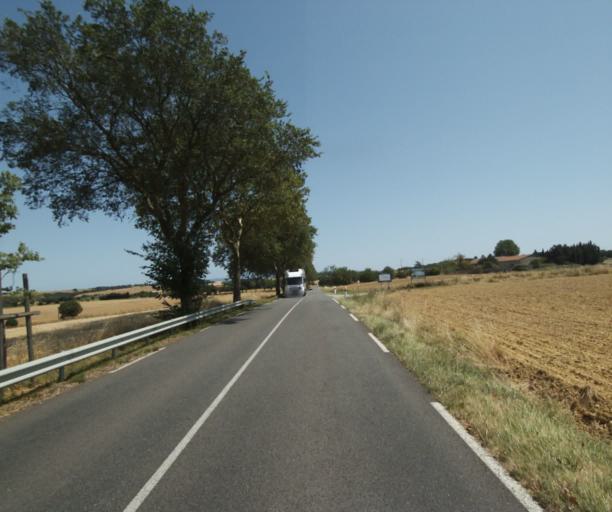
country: FR
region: Midi-Pyrenees
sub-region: Departement de la Haute-Garonne
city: Saint-Felix-Lauragais
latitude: 43.4608
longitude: 1.8442
